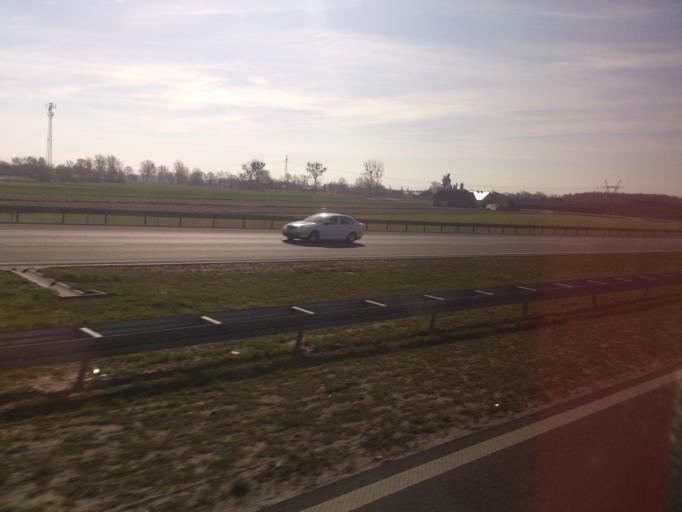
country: PL
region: Kujawsko-Pomorskie
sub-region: Powiat aleksandrowski
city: Waganiec
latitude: 52.7881
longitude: 18.8416
